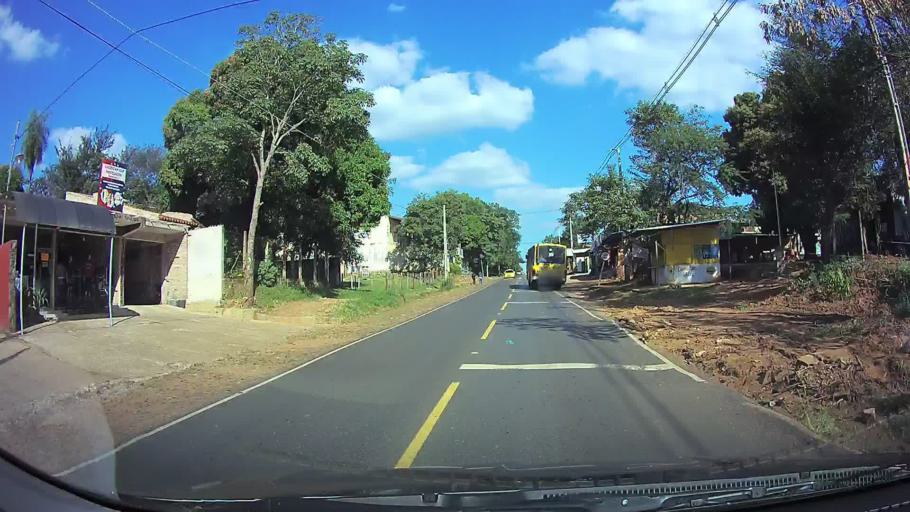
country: PY
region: Central
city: Limpio
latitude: -25.2311
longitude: -57.4760
